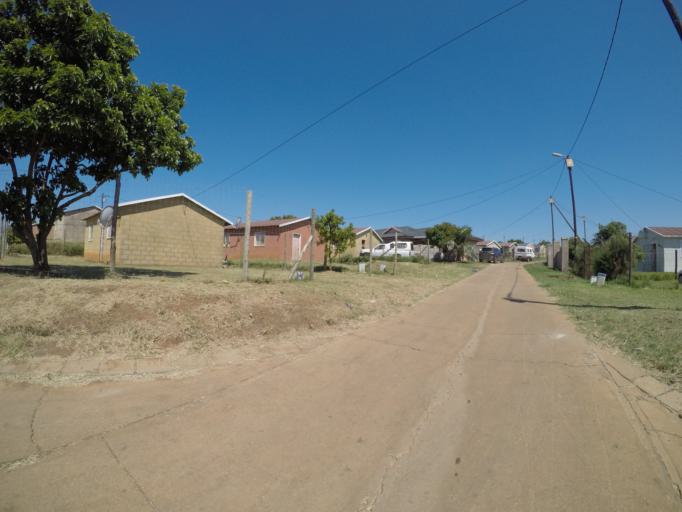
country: ZA
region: KwaZulu-Natal
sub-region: uThungulu District Municipality
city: Empangeni
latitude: -28.7665
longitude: 31.8783
